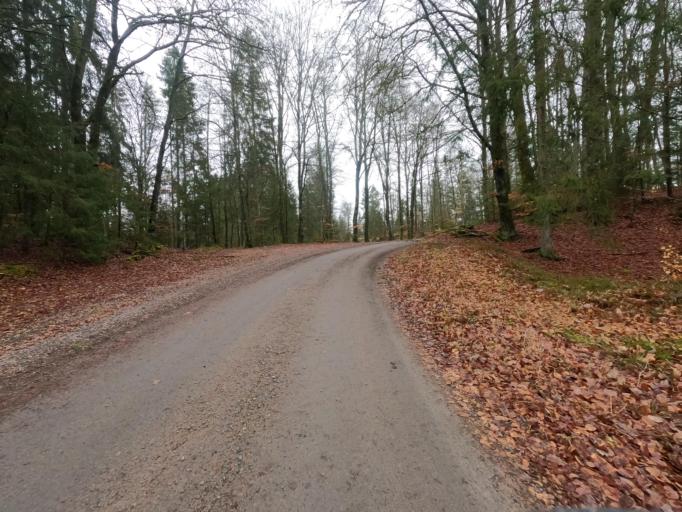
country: SE
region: Kronoberg
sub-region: Markaryds Kommun
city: Stromsnasbruk
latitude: 56.8270
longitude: 13.5648
